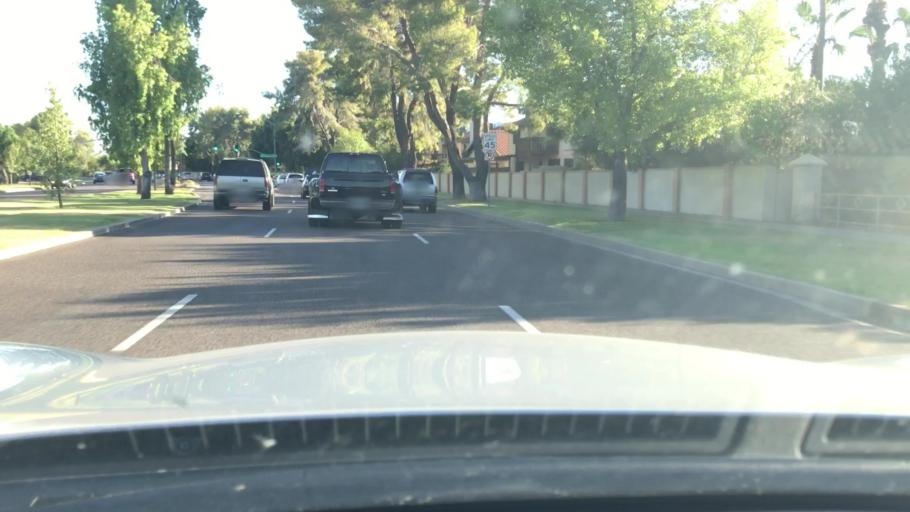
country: US
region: Arizona
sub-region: Maricopa County
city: San Carlos
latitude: 33.3733
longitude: -111.8803
